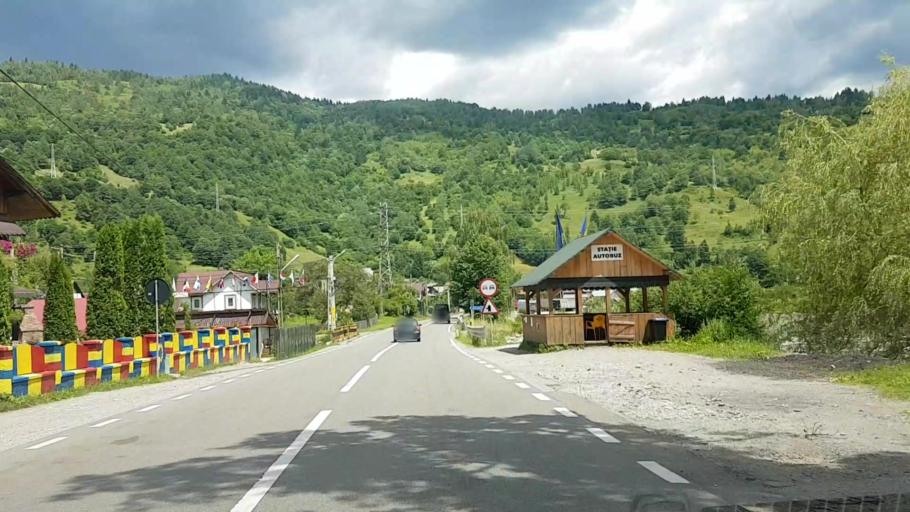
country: RO
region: Suceava
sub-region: Comuna Brosteni
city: Brosteni
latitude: 47.2591
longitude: 25.6815
